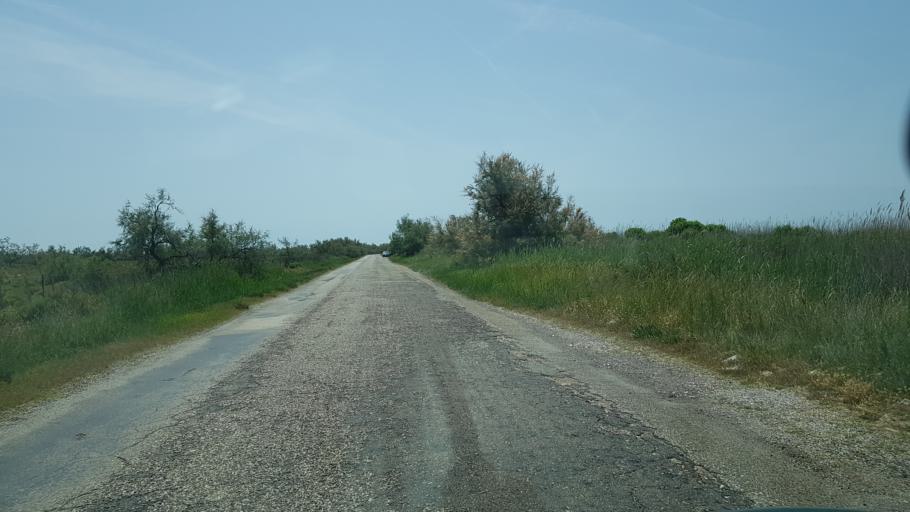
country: FR
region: Provence-Alpes-Cote d'Azur
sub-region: Departement des Bouches-du-Rhone
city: Arles
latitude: 43.5523
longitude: 4.6276
